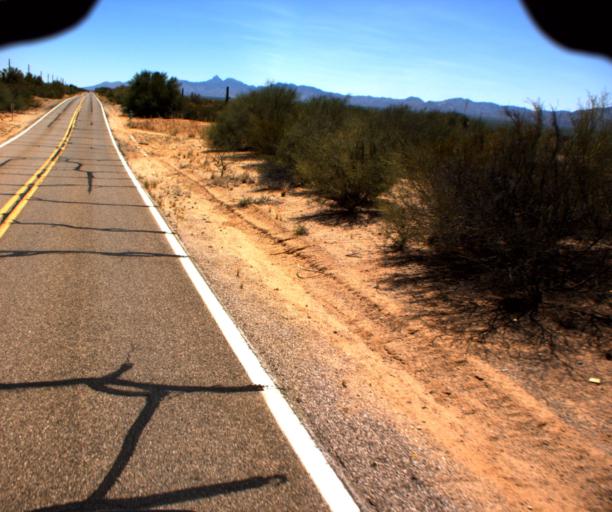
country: US
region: Arizona
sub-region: Pima County
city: Three Points
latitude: 32.0079
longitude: -111.3570
